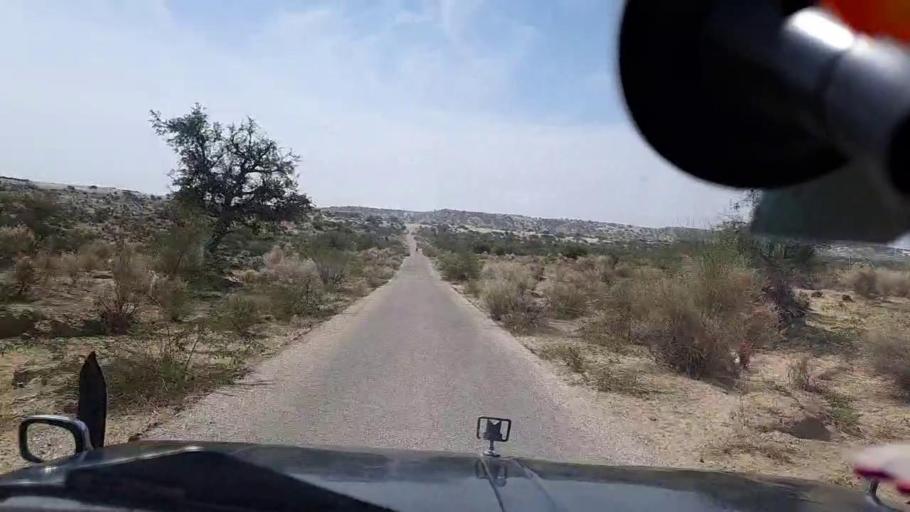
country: PK
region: Sindh
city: Diplo
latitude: 24.3782
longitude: 69.5843
